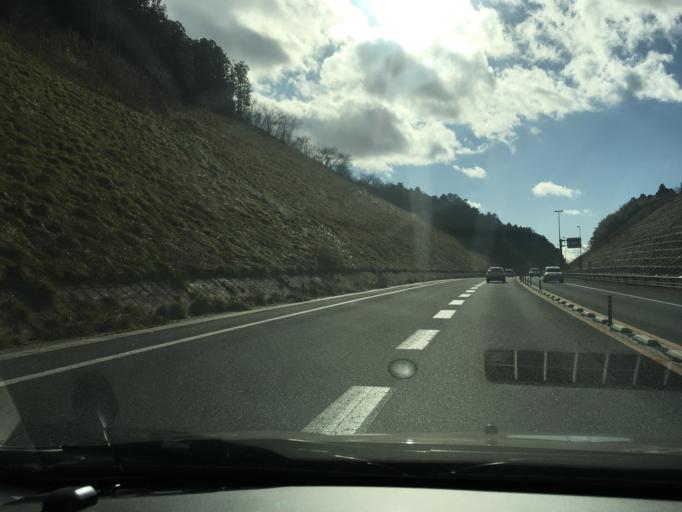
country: JP
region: Miyagi
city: Wakuya
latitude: 38.5956
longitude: 141.2818
